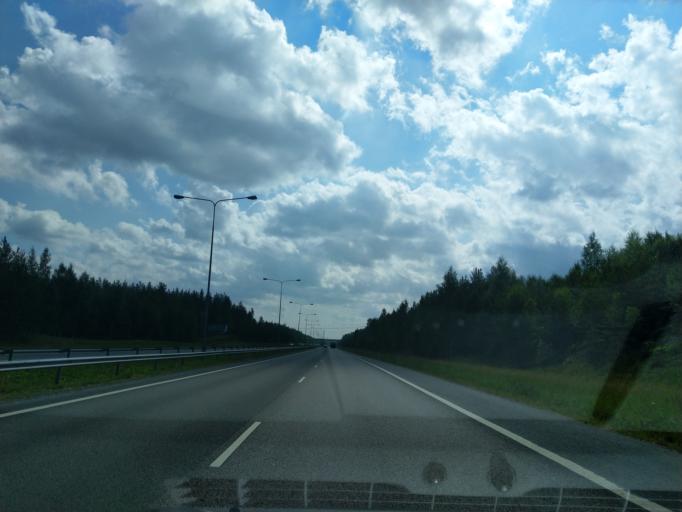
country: FI
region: South Karelia
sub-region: Imatra
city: Ruokolahti
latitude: 61.2494
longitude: 28.8756
